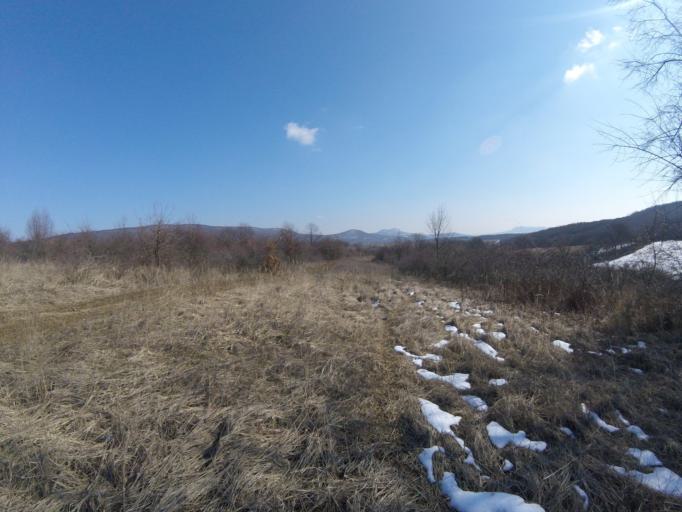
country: HU
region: Pest
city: Pilisszanto
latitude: 47.6629
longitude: 18.8669
